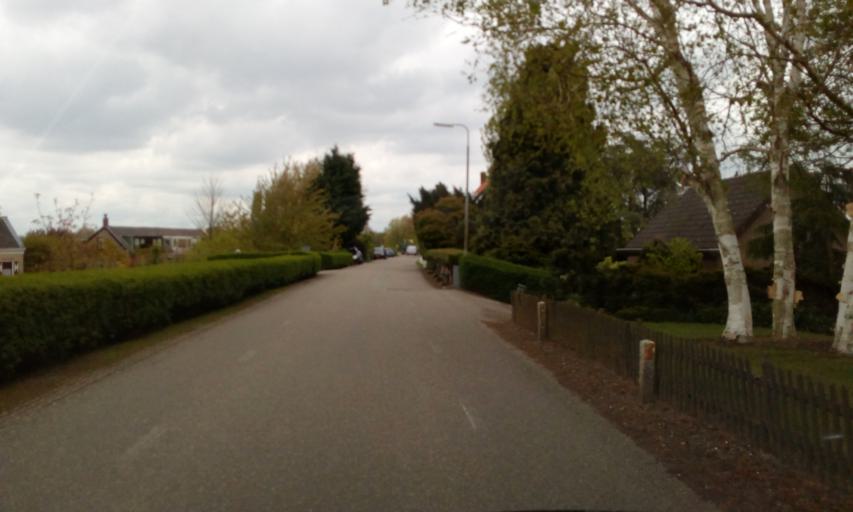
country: NL
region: South Holland
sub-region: Gemeente Zwijndrecht
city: Heerjansdam
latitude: 51.8425
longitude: 4.5638
